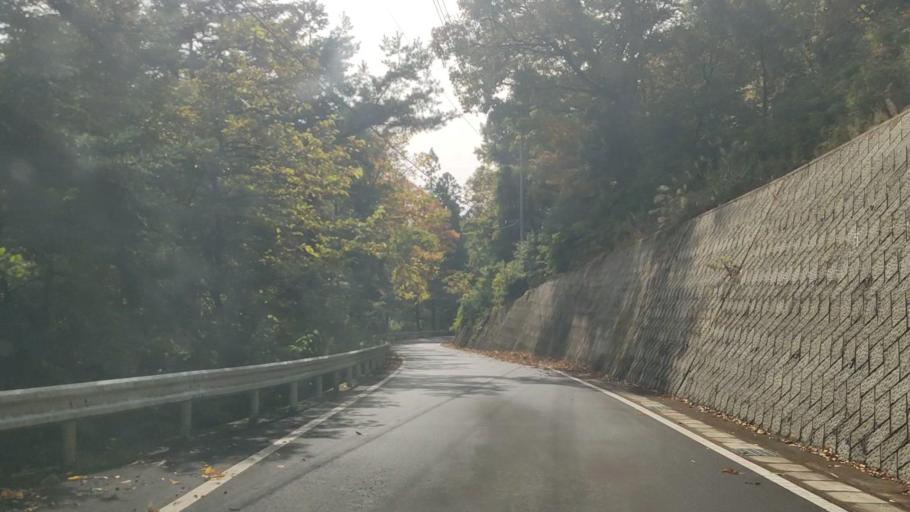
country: JP
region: Yamanashi
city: Ryuo
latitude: 35.4456
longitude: 138.4487
